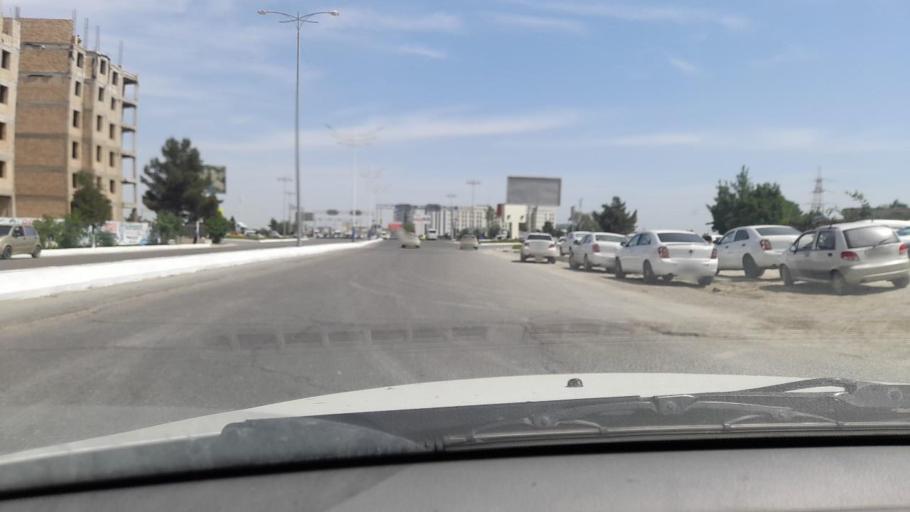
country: UZ
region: Bukhara
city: Bukhara
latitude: 39.8017
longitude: 64.4267
